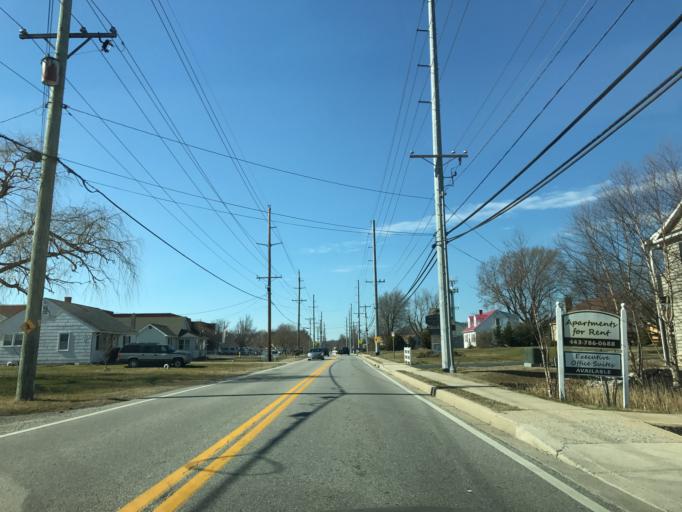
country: US
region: Maryland
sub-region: Queen Anne's County
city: Stevensville
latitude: 38.9777
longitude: -76.3069
